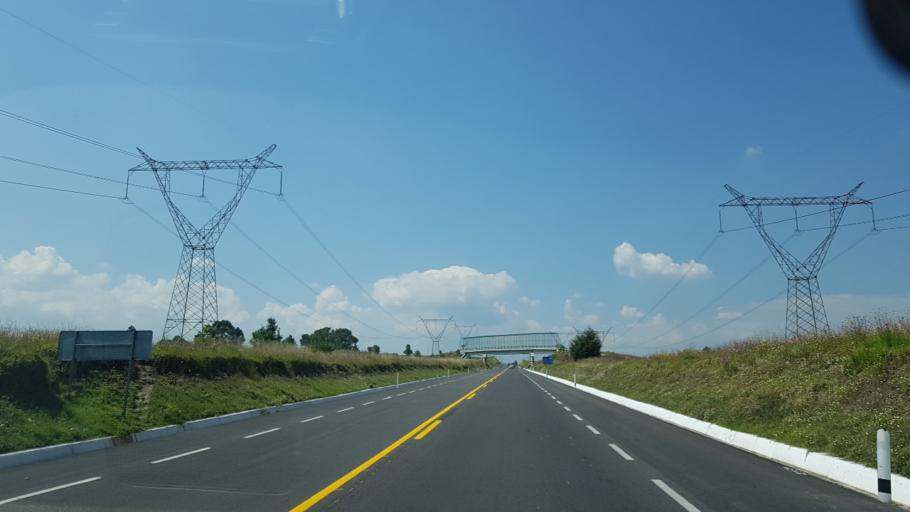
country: MX
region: Mexico
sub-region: Almoloya de Juarez
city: San Pedro de la Hortaliza (Ejido Almoloyan)
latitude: 19.3797
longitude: -99.8235
